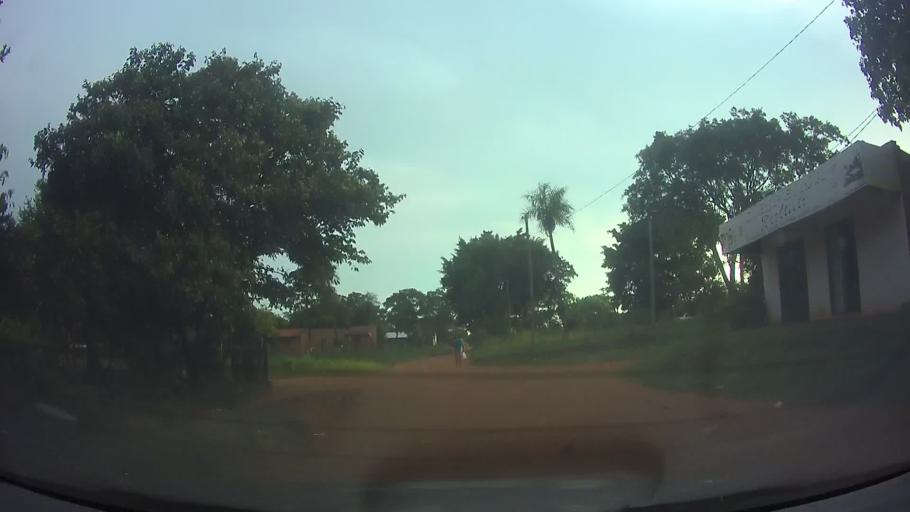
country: PY
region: Central
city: Limpio
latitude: -25.2437
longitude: -57.4493
